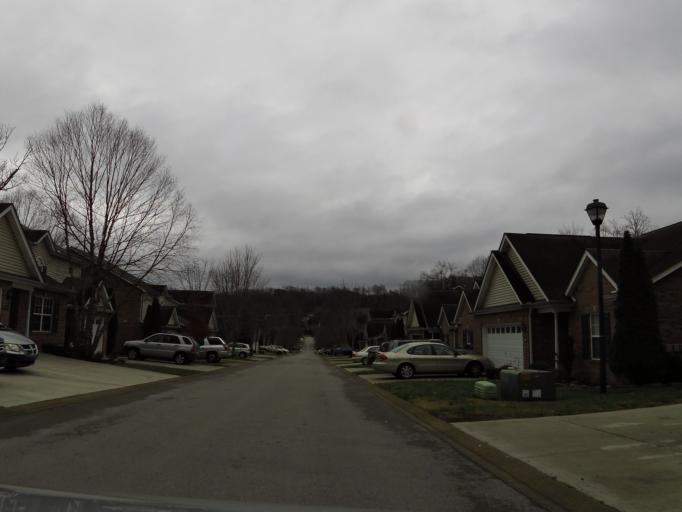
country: US
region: Tennessee
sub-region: Knox County
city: Knoxville
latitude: 35.9983
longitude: -84.0398
